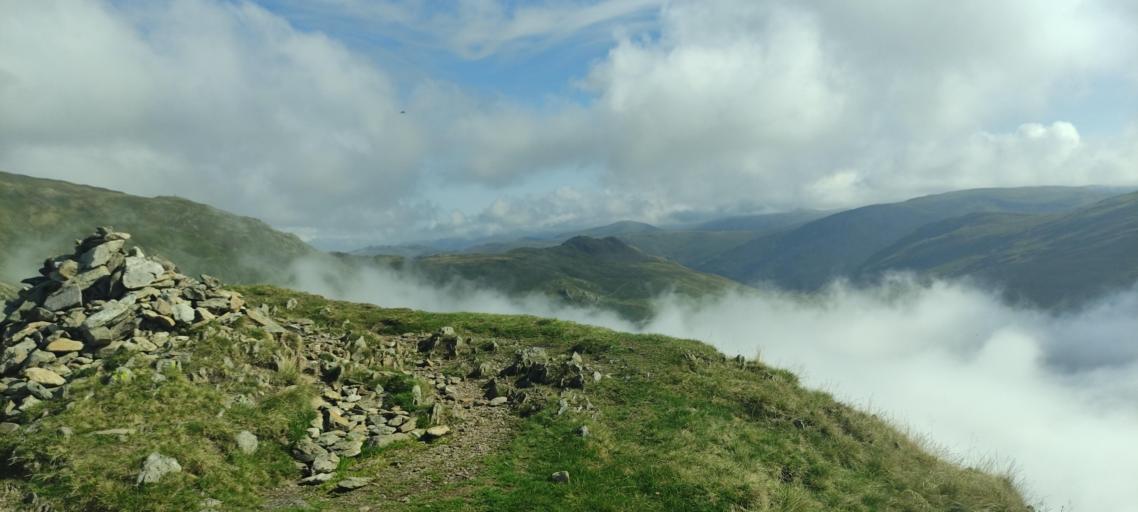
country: GB
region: England
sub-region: Cumbria
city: Ambleside
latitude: 54.4710
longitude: -2.9668
